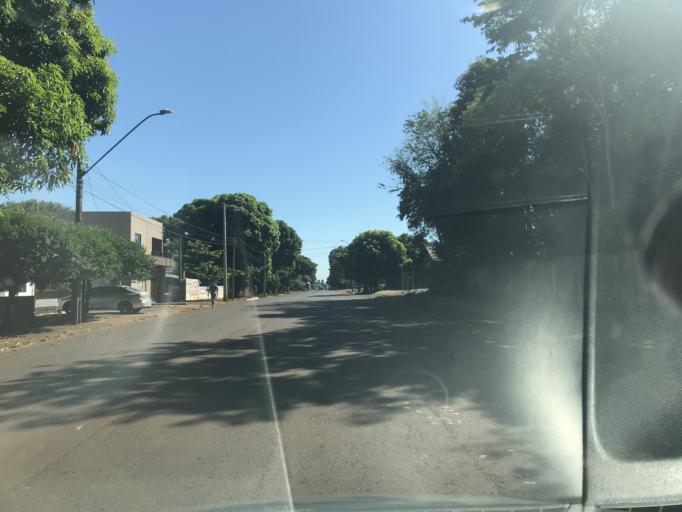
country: BR
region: Parana
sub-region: Palotina
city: Palotina
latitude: -24.2733
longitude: -53.8451
